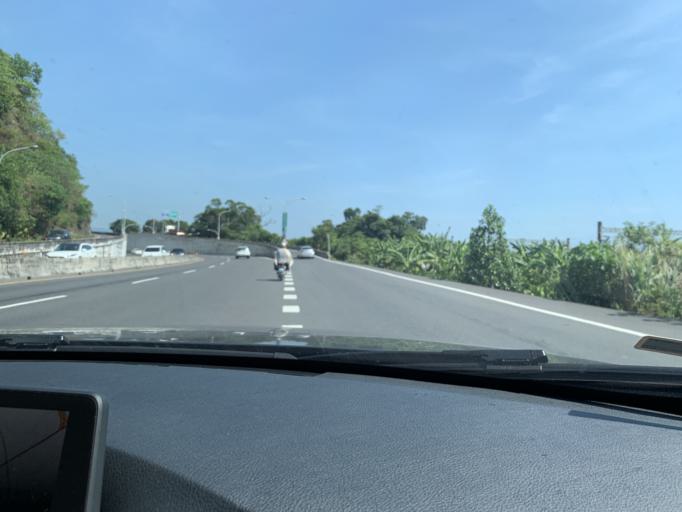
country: TW
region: Taiwan
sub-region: Yilan
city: Yilan
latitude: 24.6123
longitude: 121.8254
